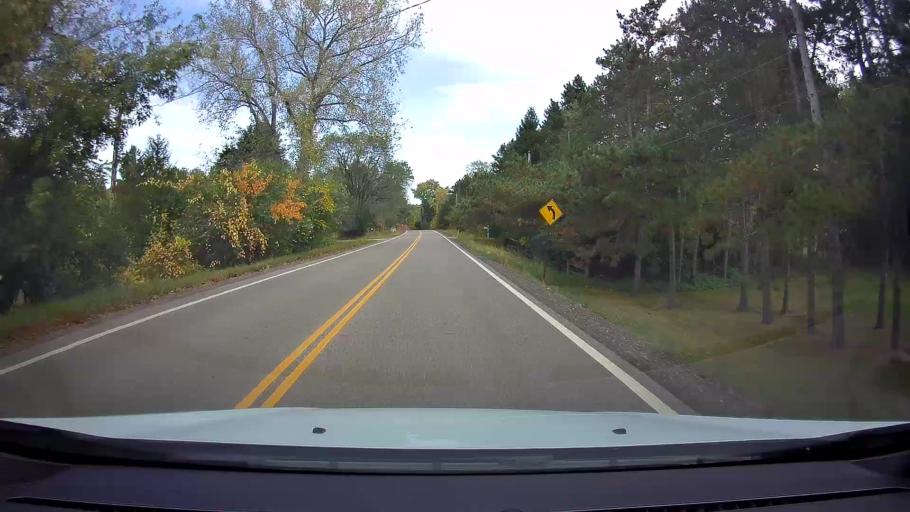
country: US
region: Minnesota
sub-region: Washington County
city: Stillwater
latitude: 45.0806
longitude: -92.8265
